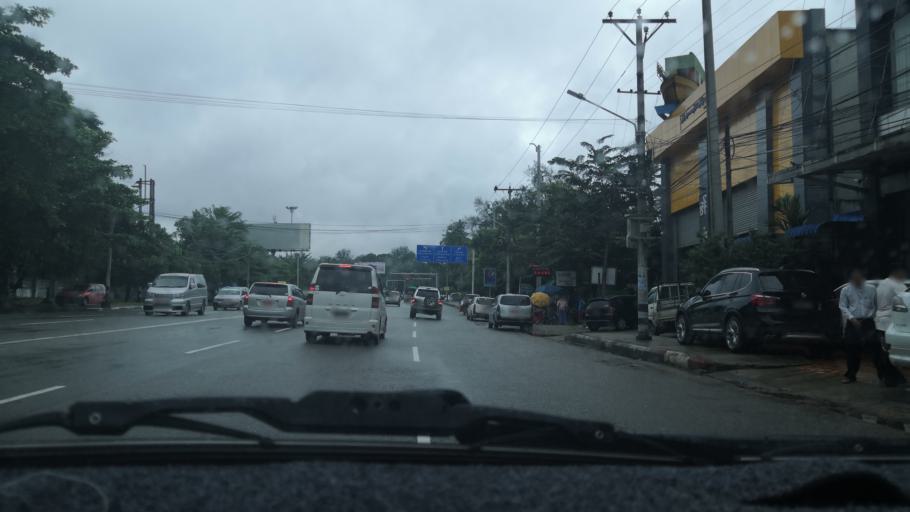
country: MM
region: Yangon
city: Yangon
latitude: 16.8888
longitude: 96.1229
